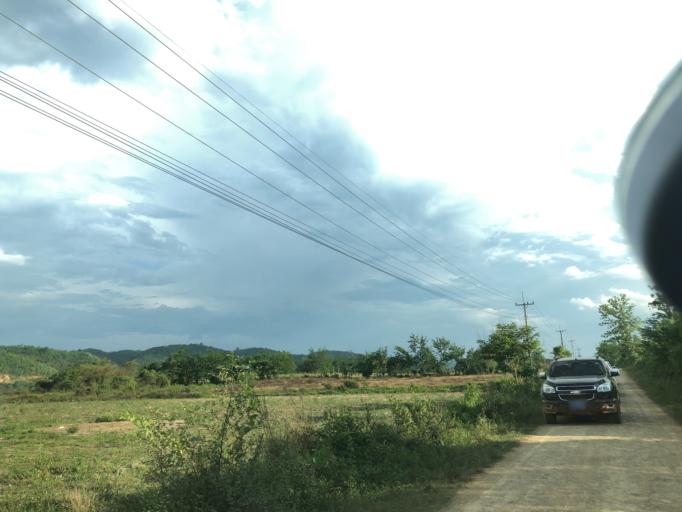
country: LA
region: Xiagnabouli
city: Muang Kenthao
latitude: 17.9897
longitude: 101.4183
